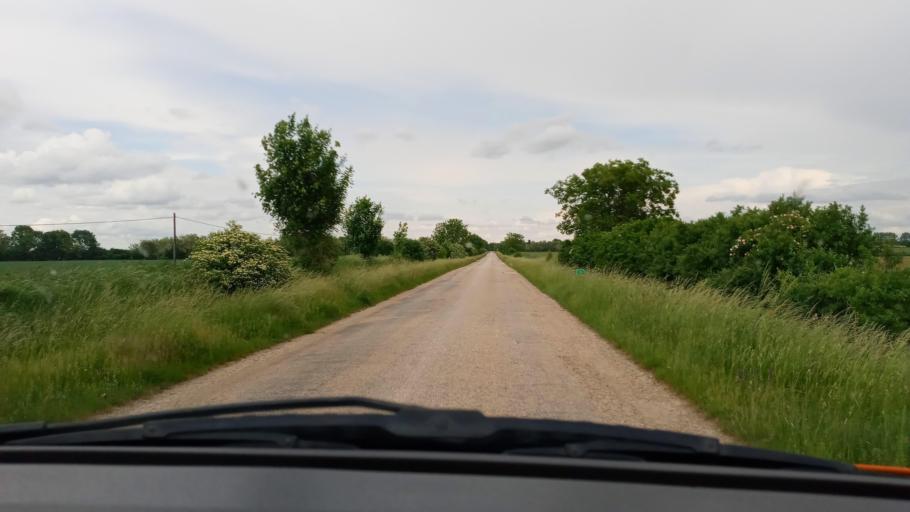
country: HU
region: Baranya
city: Harkany
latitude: 45.9139
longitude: 18.1472
